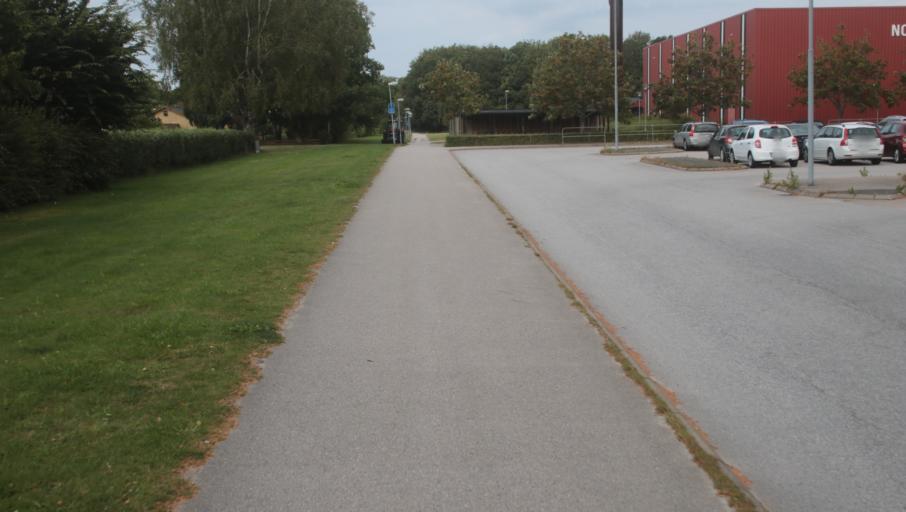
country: SE
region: Blekinge
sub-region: Karlshamns Kommun
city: Morrum
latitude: 56.1995
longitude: 14.7570
